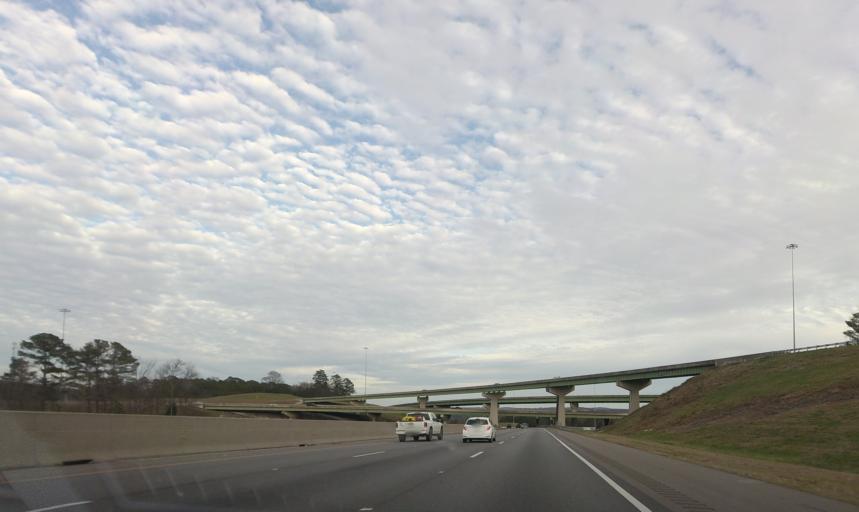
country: US
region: Alabama
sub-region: Jefferson County
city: Irondale
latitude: 33.5447
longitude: -86.6456
